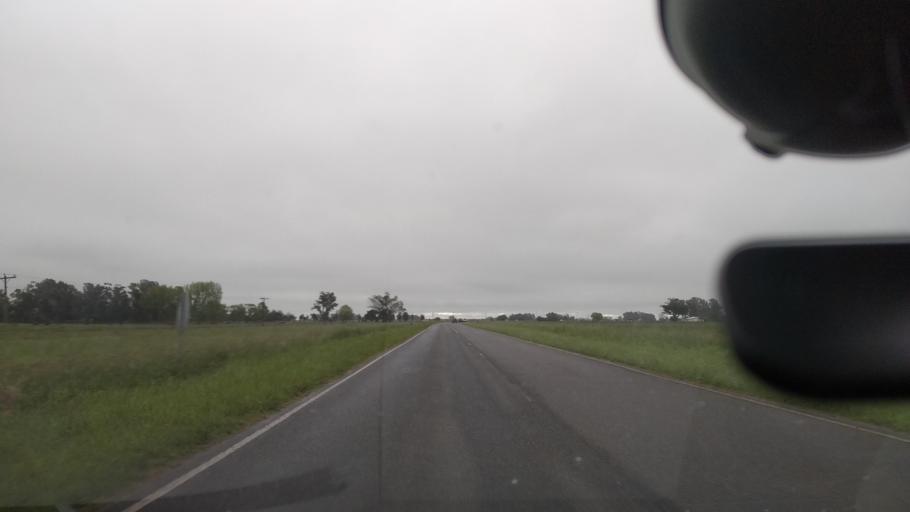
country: AR
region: Buenos Aires
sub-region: Partido de Magdalena
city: Magdalena
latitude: -35.2264
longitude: -57.7252
